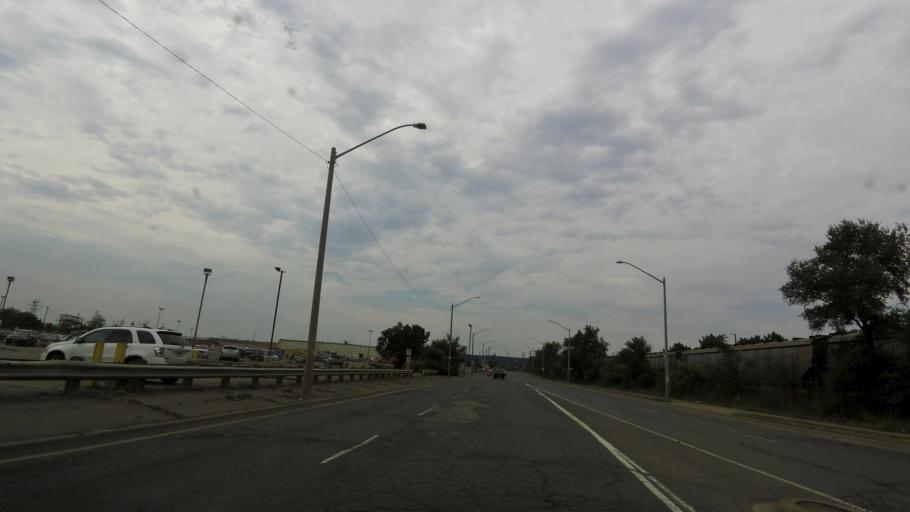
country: CA
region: Ontario
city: Hamilton
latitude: 43.2605
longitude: -79.8096
